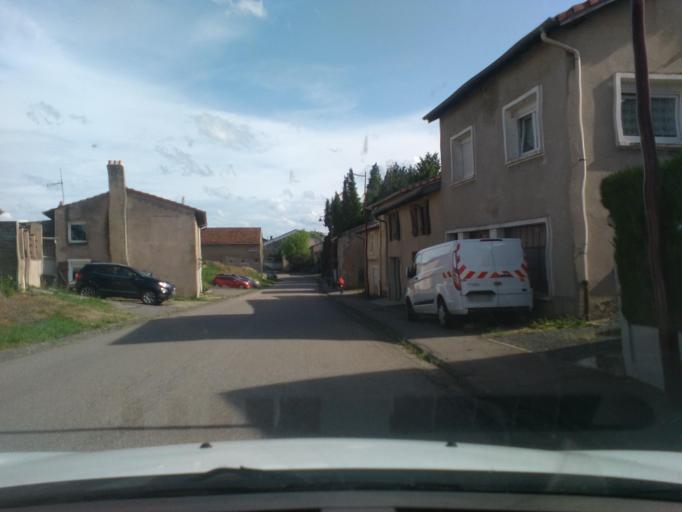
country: FR
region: Lorraine
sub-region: Departement de Meurthe-et-Moselle
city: Baccarat
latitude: 48.5485
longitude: 6.7237
